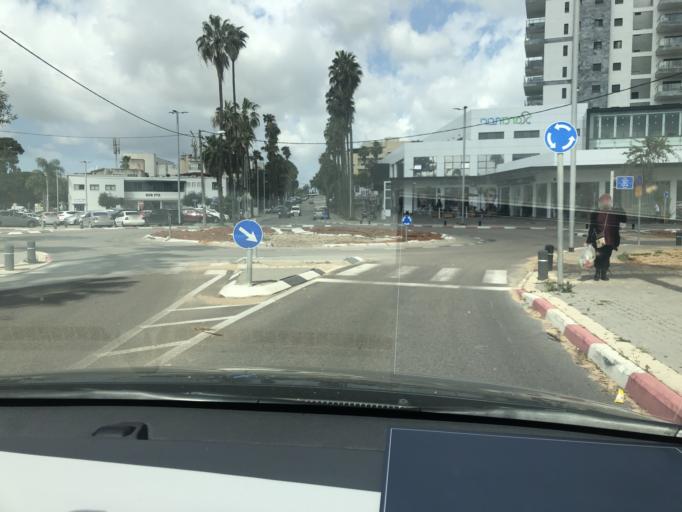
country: IL
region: Haifa
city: Hadera
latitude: 32.4724
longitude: 34.9745
